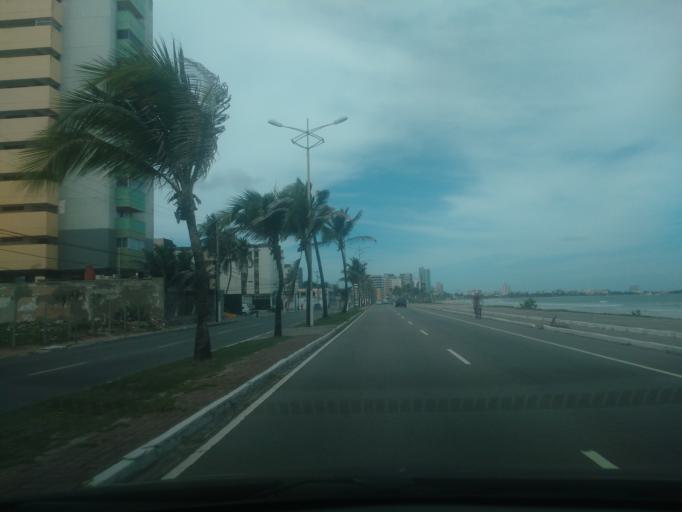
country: BR
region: Alagoas
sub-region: Maceio
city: Maceio
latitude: -9.6723
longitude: -35.7462
